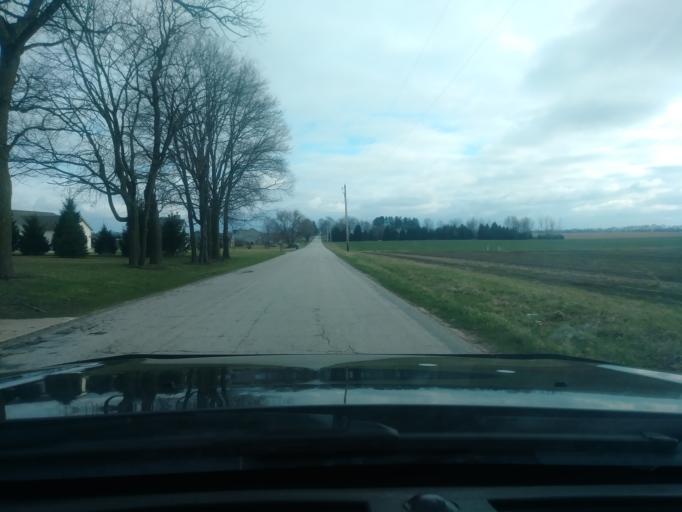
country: US
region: Indiana
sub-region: LaPorte County
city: LaPorte
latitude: 41.5877
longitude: -86.7980
